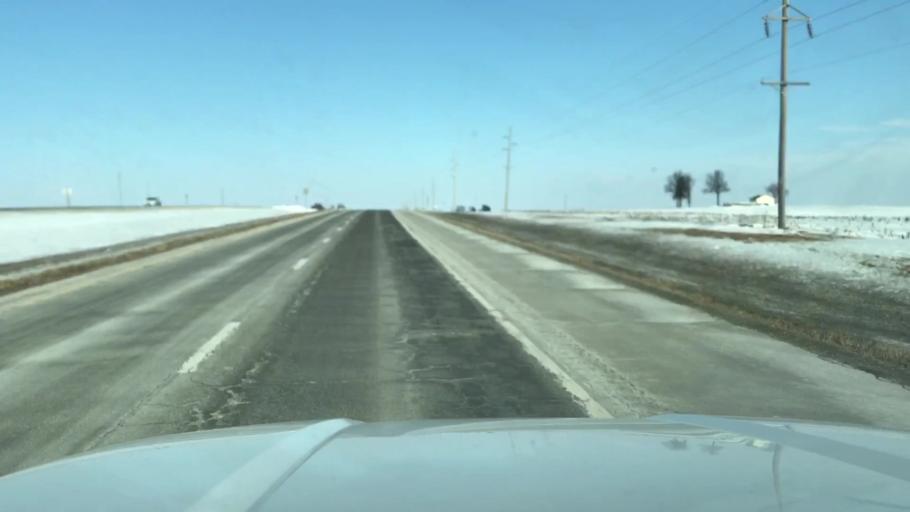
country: US
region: Missouri
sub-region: Nodaway County
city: Maryville
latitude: 40.2275
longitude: -94.8677
